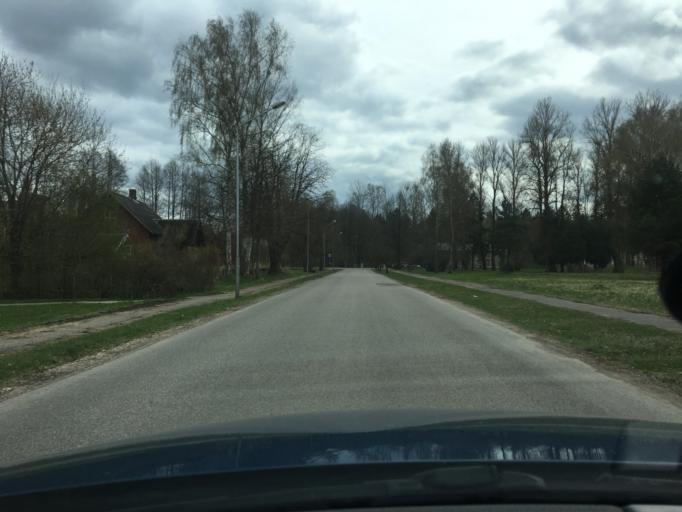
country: LV
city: Tireli
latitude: 56.9428
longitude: 23.4910
